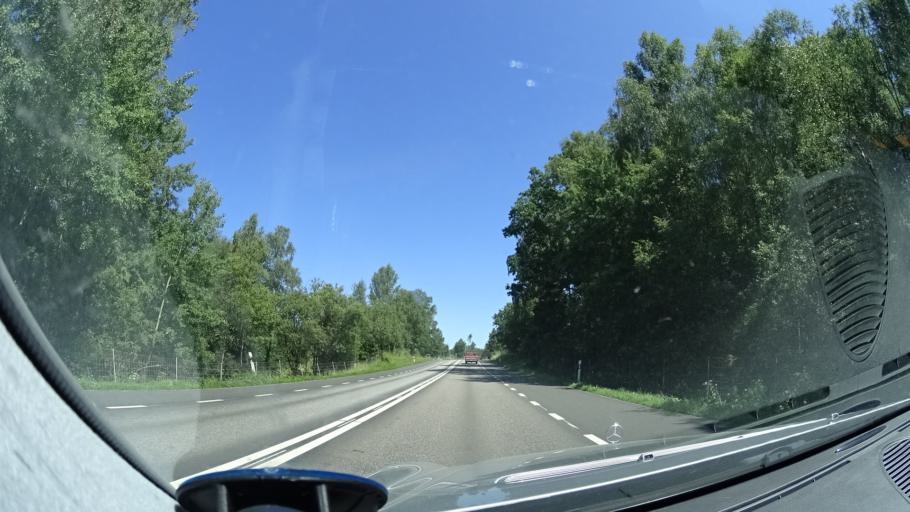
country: SE
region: Skane
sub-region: Horby Kommun
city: Hoerby
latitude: 55.9258
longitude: 13.7951
